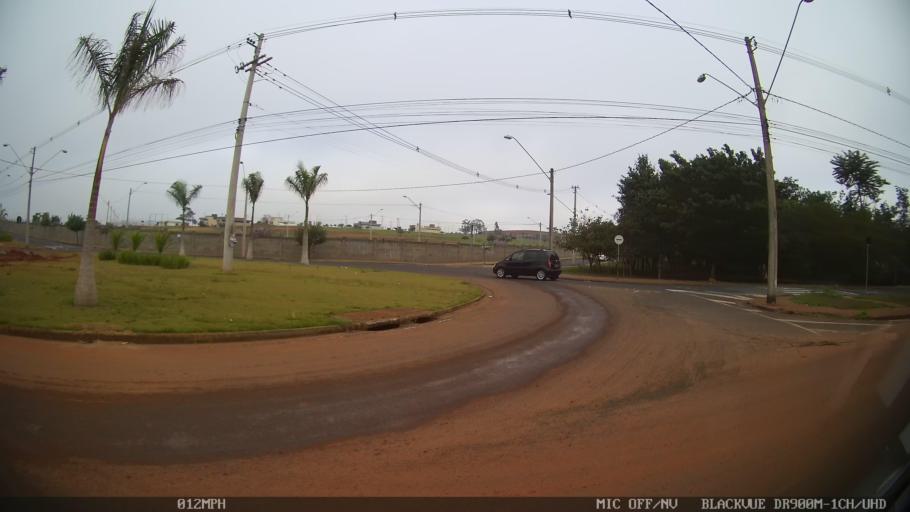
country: BR
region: Sao Paulo
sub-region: Sao Jose Do Rio Preto
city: Sao Jose do Rio Preto
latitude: -20.8492
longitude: -49.3702
